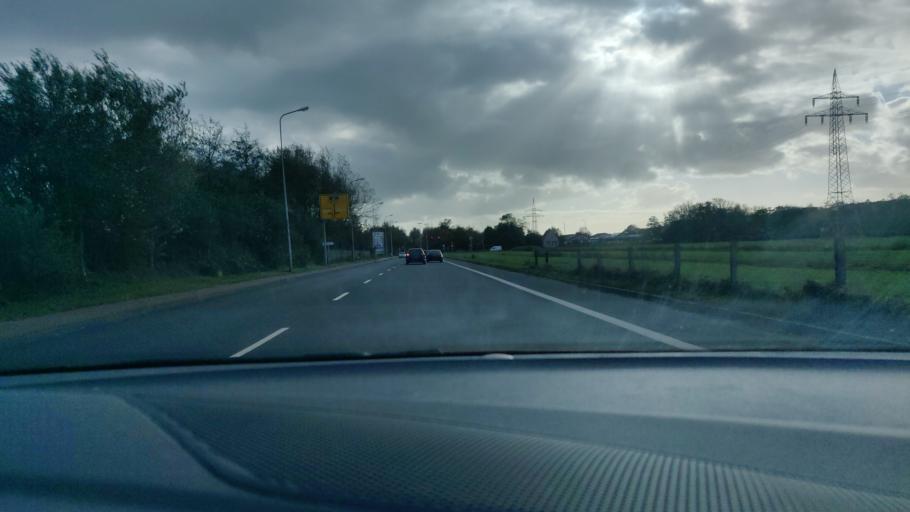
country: DE
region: Lower Saxony
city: Cuxhaven
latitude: 53.8622
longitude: 8.6739
